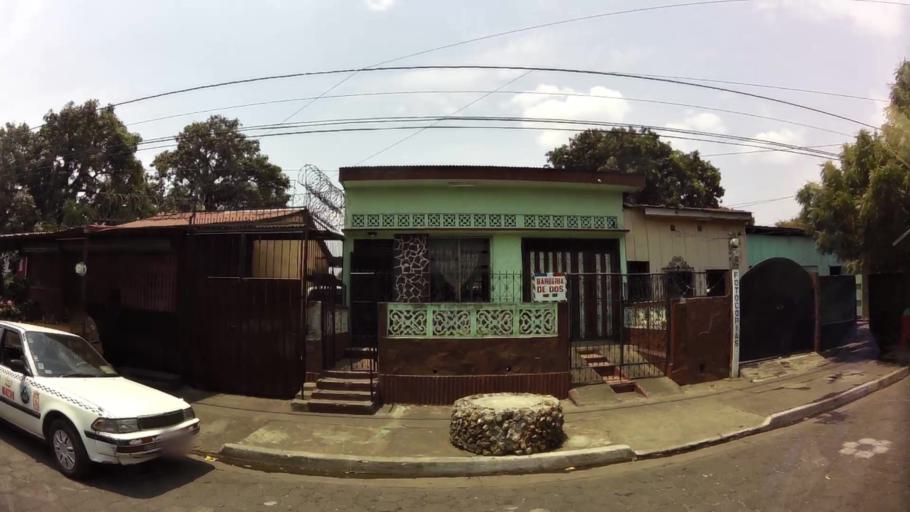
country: NI
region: Managua
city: Ciudad Sandino
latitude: 12.1511
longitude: -86.3014
